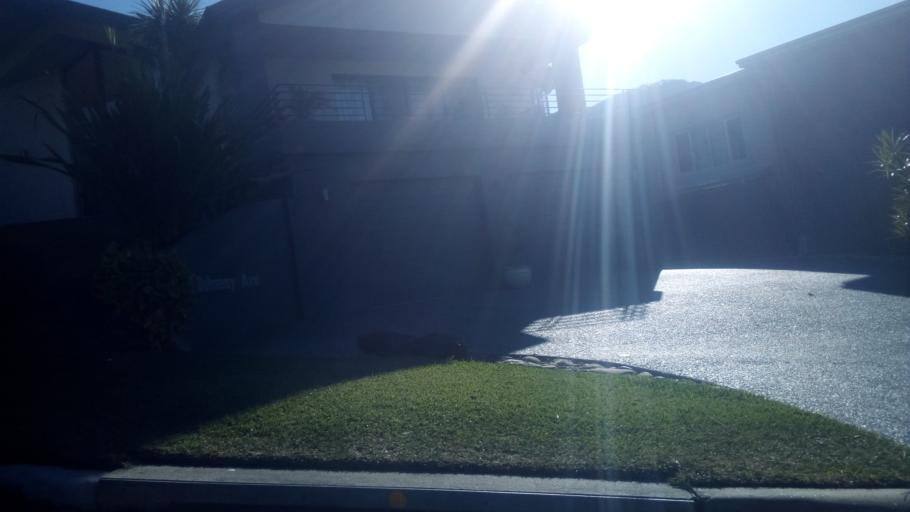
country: AU
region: New South Wales
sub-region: Wollongong
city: Mount Keira
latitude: -34.4167
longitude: 150.8488
